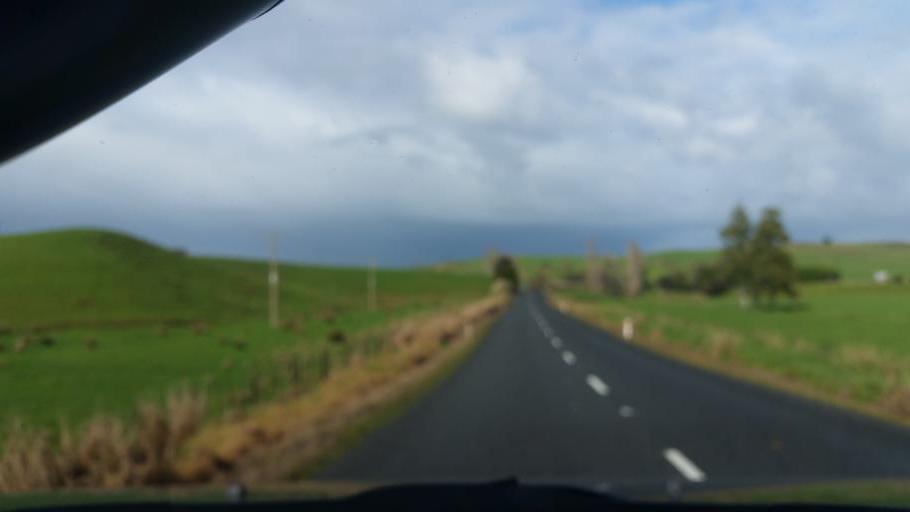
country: NZ
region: Northland
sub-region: Kaipara District
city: Dargaville
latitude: -35.8167
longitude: 173.9255
